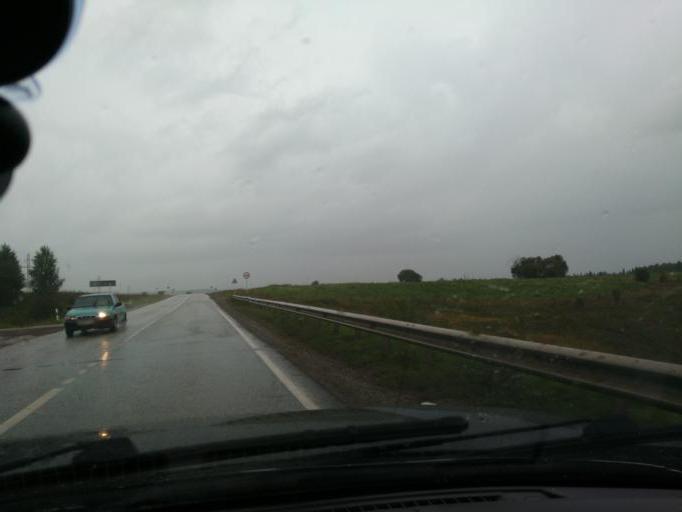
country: RU
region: Perm
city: Barda
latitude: 57.0934
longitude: 55.5349
